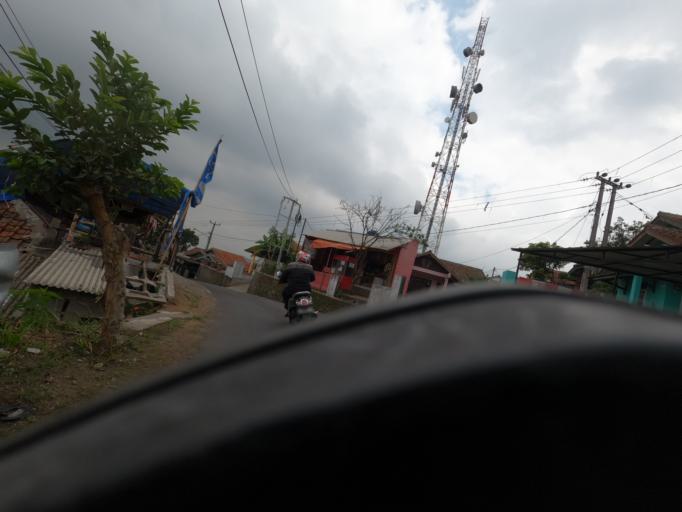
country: ID
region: West Java
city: Cimahi
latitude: -6.8163
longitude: 107.5449
